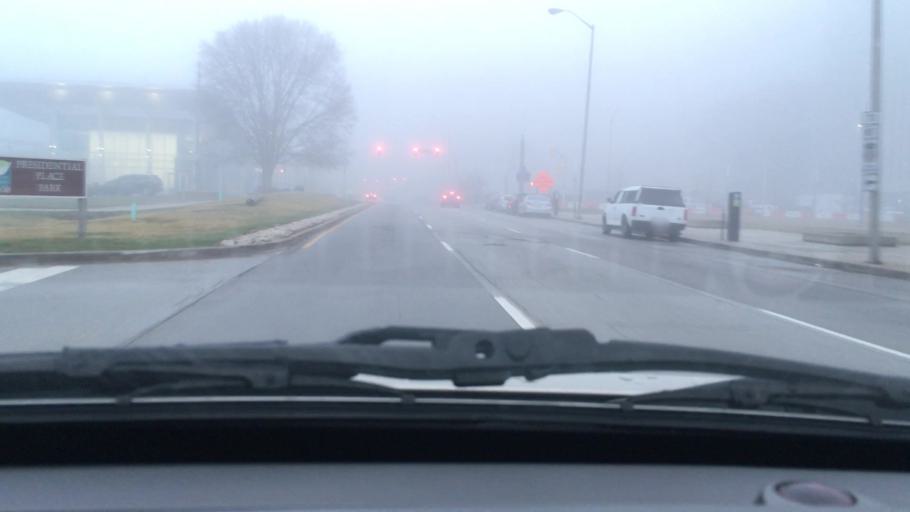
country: US
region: Indiana
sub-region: Marion County
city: Indianapolis
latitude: 39.7670
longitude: -86.1515
